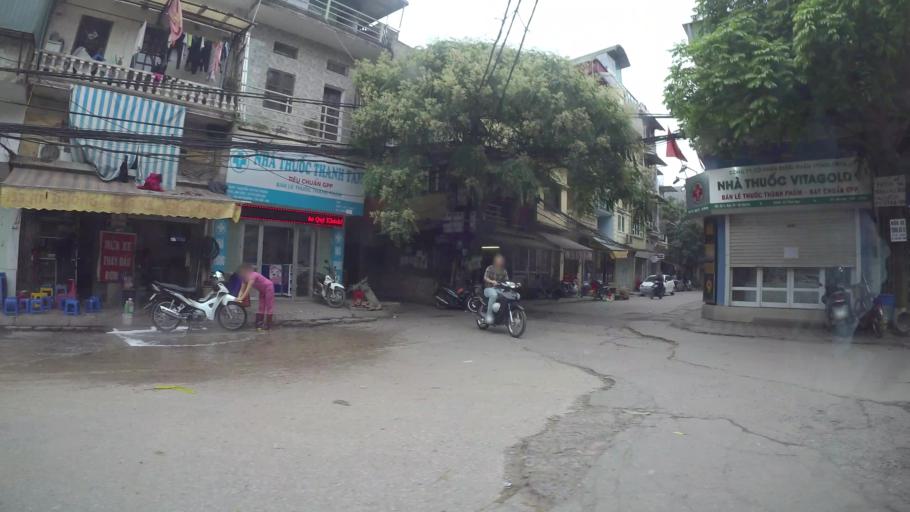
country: VN
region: Ha Noi
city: Hoan Kiem
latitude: 21.0549
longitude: 105.8395
